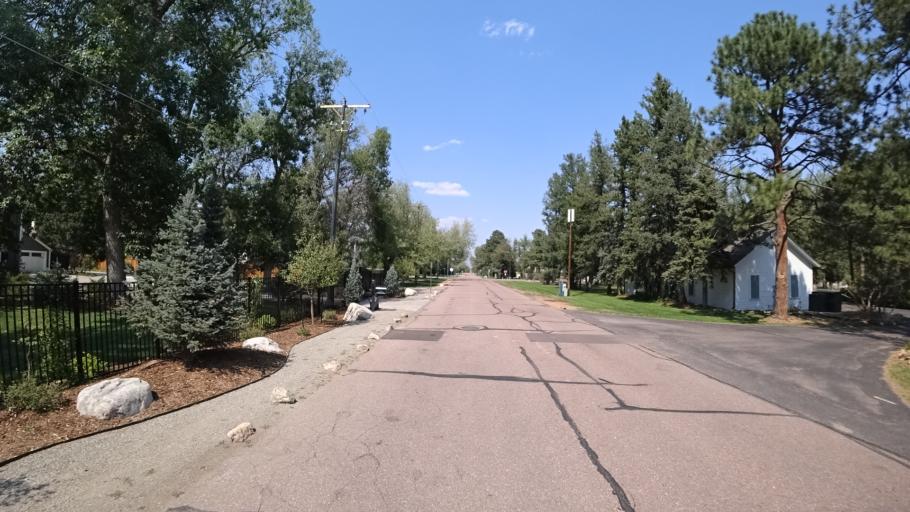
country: US
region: Colorado
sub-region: El Paso County
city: Colorado Springs
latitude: 38.7913
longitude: -104.8451
